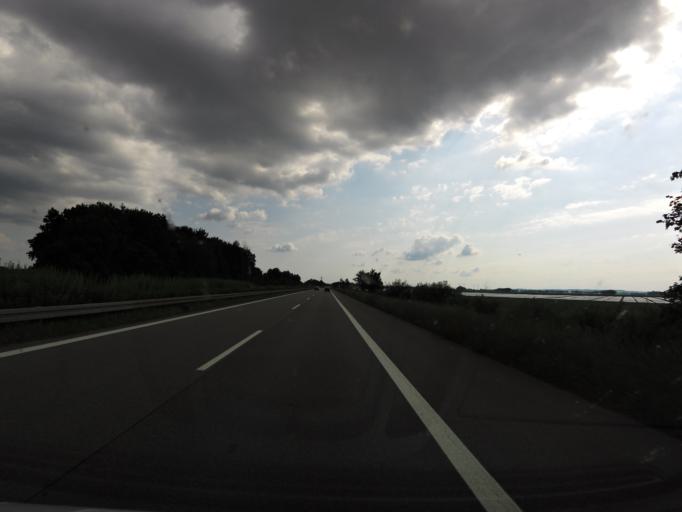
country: DE
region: Bavaria
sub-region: Lower Bavaria
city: Wallersdorf
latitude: 48.7603
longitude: 12.7703
